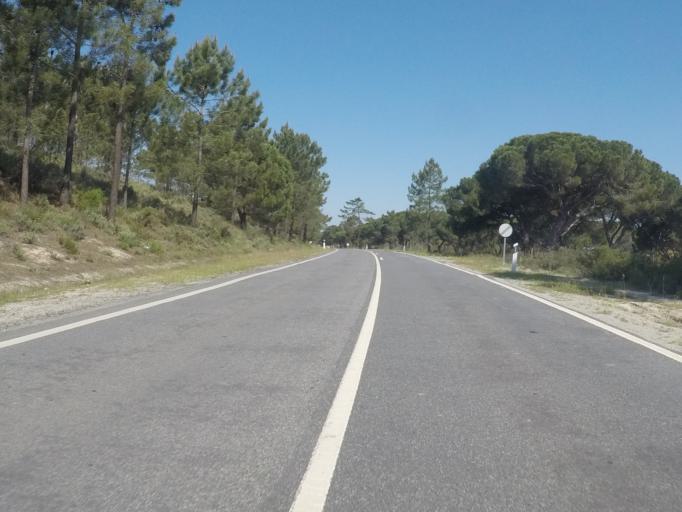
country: PT
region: Setubal
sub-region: Grandola
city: Grandola
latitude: 38.3037
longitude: -8.7359
